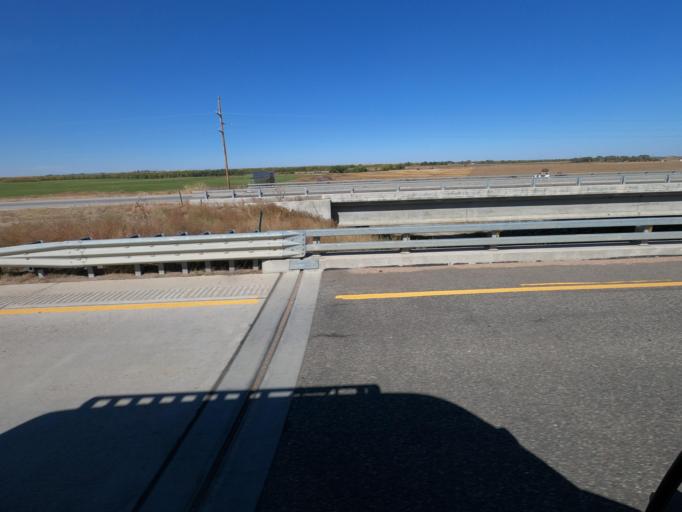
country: US
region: Colorado
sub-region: Morgan County
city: Brush
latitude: 40.2678
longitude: -103.7062
